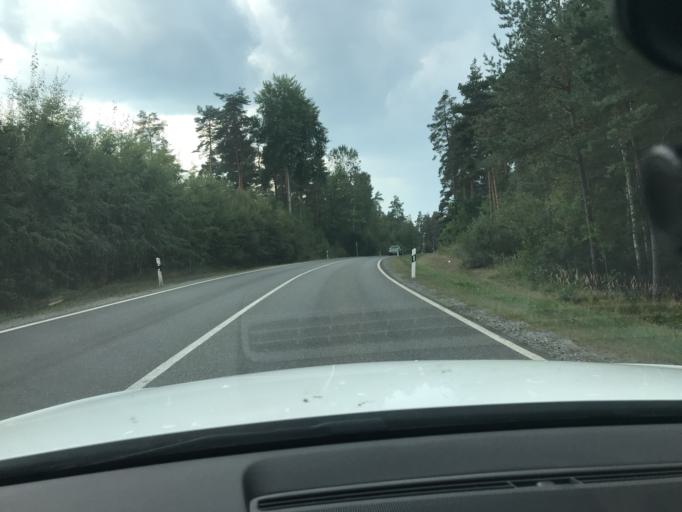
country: DE
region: Bavaria
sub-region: Upper Palatinate
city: Grafenwohr
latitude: 49.7036
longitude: 11.9314
